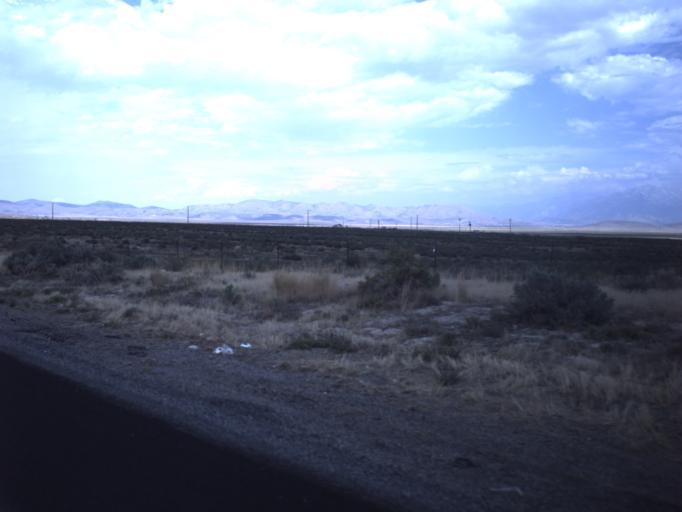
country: US
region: Utah
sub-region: Utah County
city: Eagle Mountain
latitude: 40.2861
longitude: -112.0966
